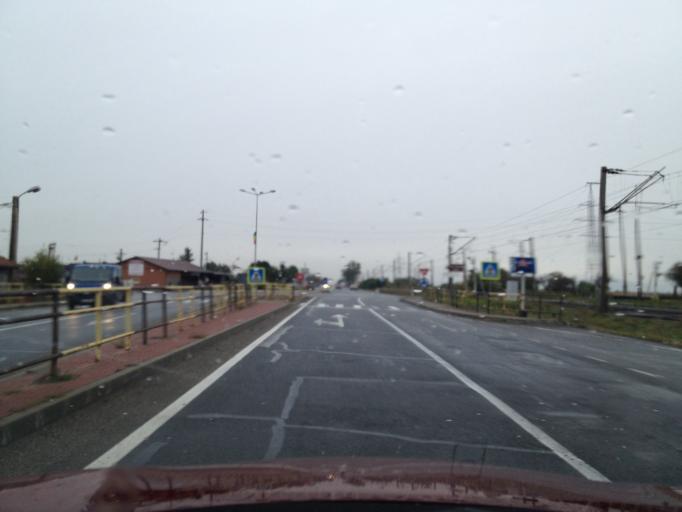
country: RO
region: Brasov
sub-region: Comuna Harman
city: Harman
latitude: 45.7005
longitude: 25.6897
